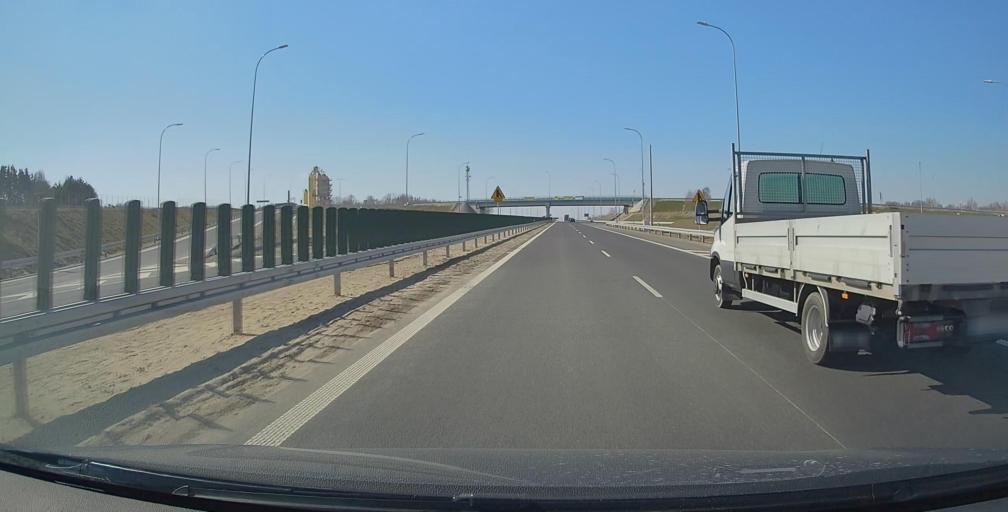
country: PL
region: Subcarpathian Voivodeship
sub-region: Powiat rzeszowski
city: Gorno
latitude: 50.3033
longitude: 22.1343
